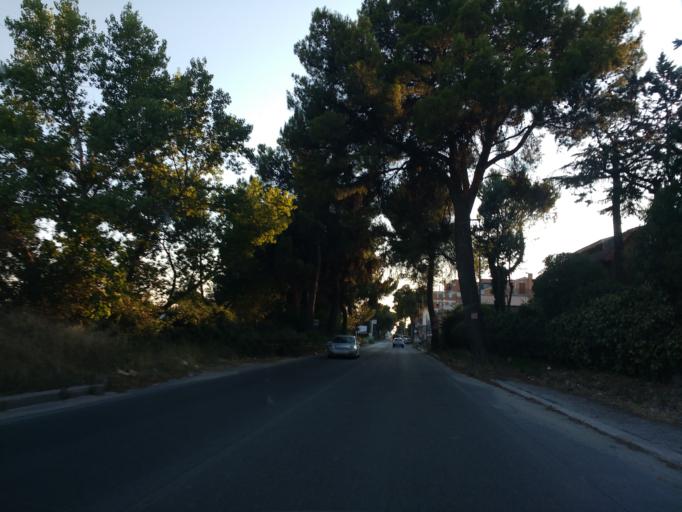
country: IT
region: Latium
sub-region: Citta metropolitana di Roma Capitale
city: Villalba
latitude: 41.9531
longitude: 12.7388
